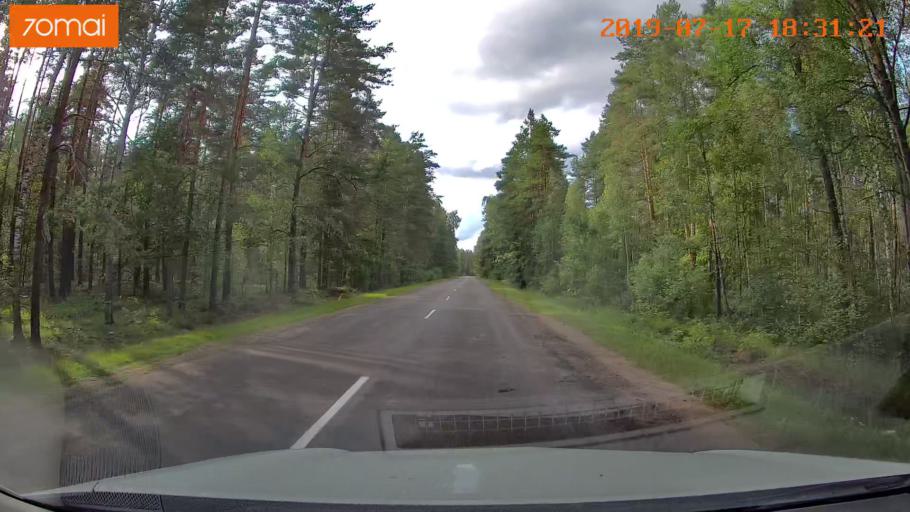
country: BY
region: Mogilev
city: Asipovichy
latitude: 53.2582
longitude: 28.6830
